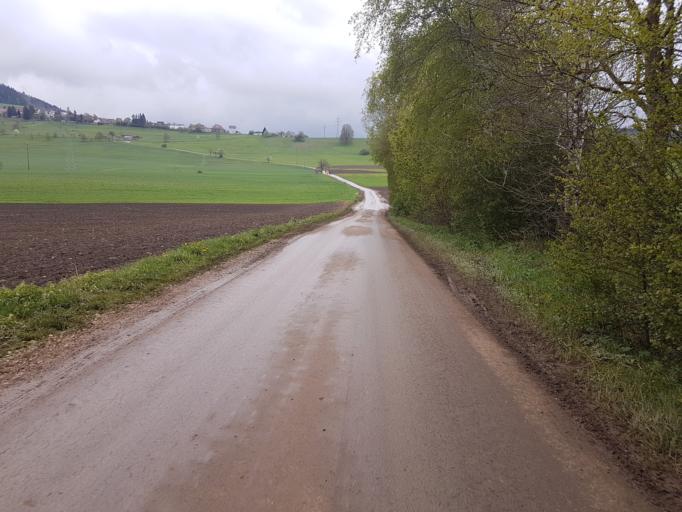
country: DE
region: Baden-Wuerttemberg
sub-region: Freiburg Region
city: Hufingen
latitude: 47.8993
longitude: 8.5409
